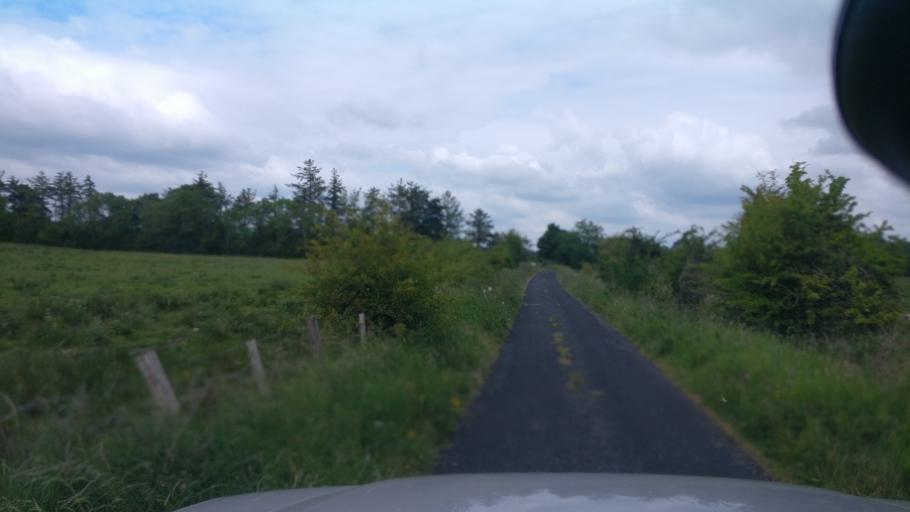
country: IE
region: Connaught
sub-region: County Galway
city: Ballinasloe
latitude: 53.2704
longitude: -8.3620
